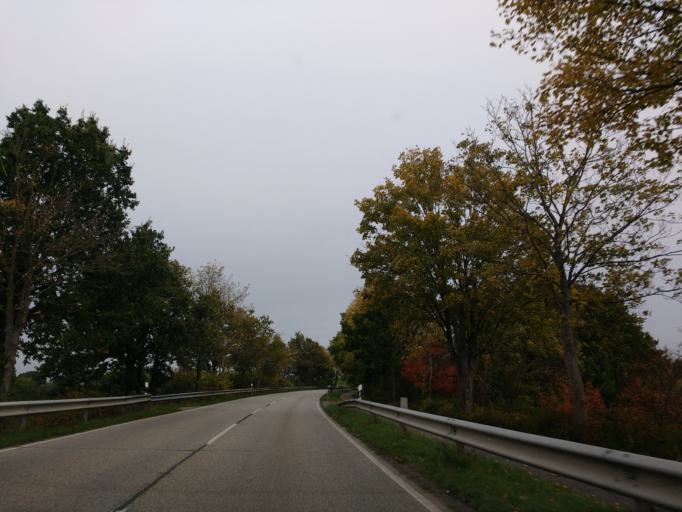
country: DE
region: Schleswig-Holstein
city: Gromitz
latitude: 54.1627
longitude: 10.9643
